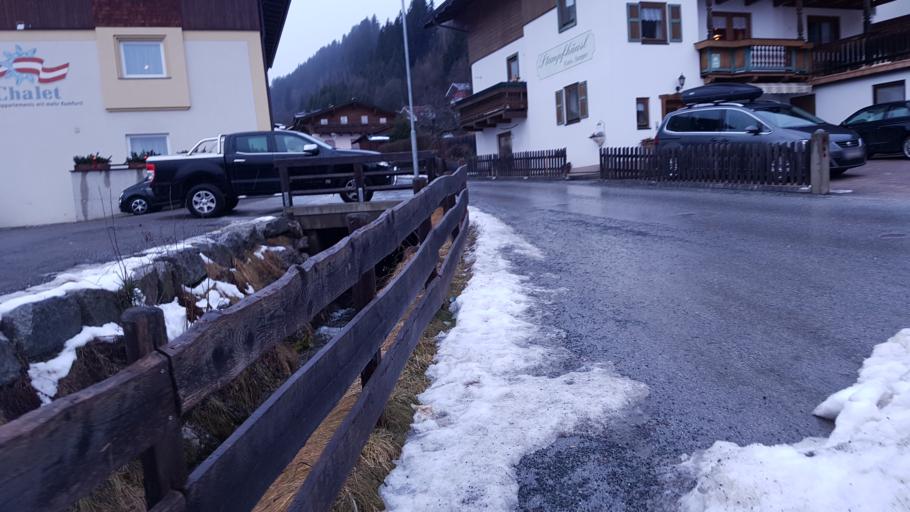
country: AT
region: Salzburg
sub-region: Politischer Bezirk Zell am See
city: Neukirchen am Grossvenediger
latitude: 47.2550
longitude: 12.2806
